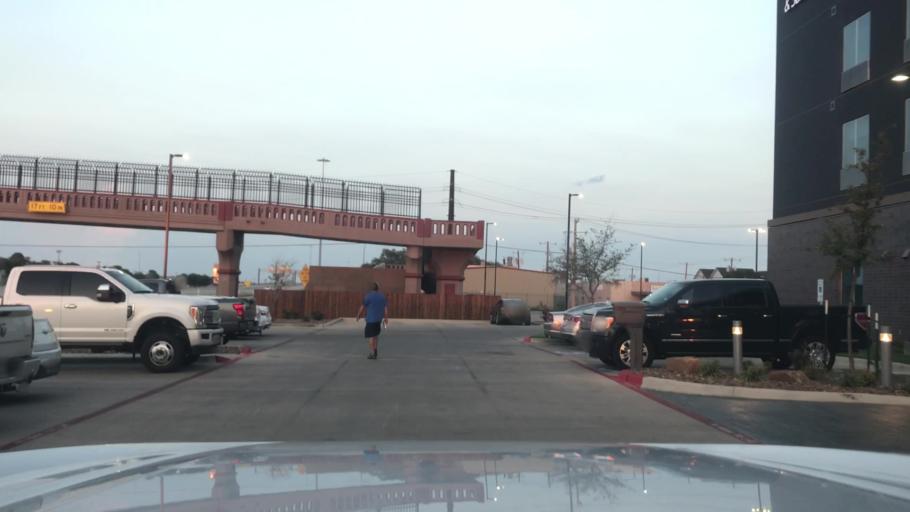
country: US
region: Texas
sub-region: Lubbock County
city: Lubbock
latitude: 33.5922
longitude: -101.8631
